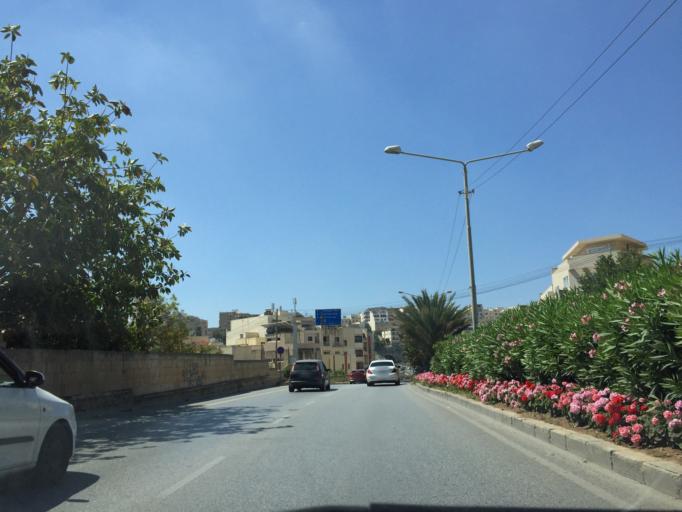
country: MT
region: Saint Julian
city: San Giljan
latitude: 35.9187
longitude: 14.4867
